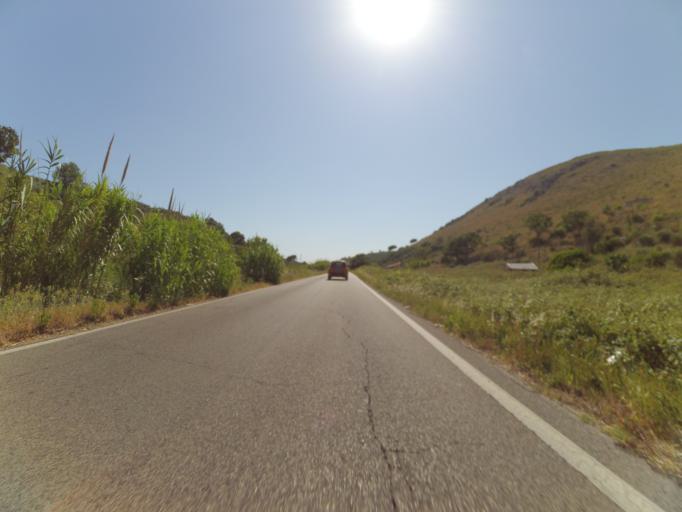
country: IT
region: Latium
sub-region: Provincia di Latina
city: Gaeta
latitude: 41.2320
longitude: 13.5158
